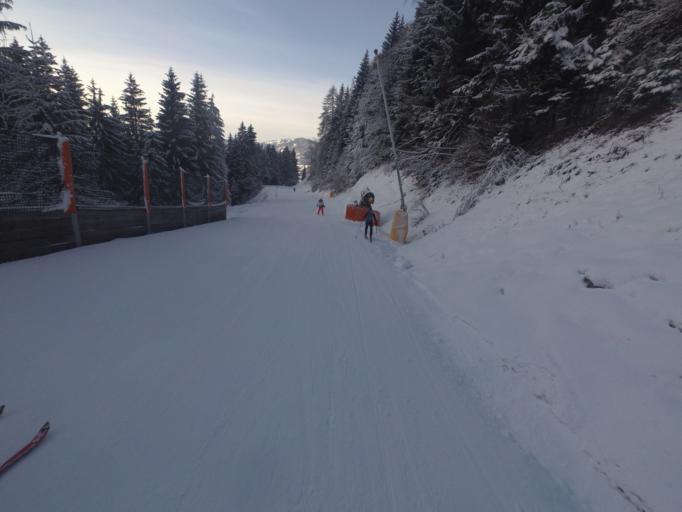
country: AT
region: Salzburg
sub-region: Politischer Bezirk Sankt Johann im Pongau
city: Sankt Johann im Pongau
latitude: 47.3172
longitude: 13.2095
